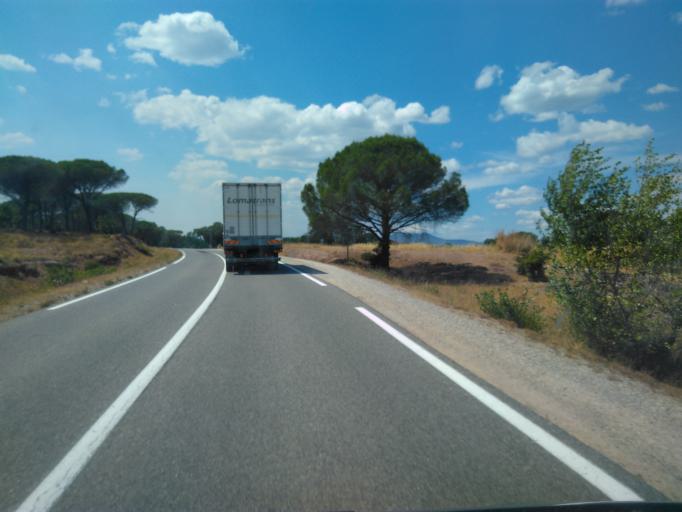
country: FR
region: Provence-Alpes-Cote d'Azur
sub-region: Departement du Var
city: La Garde-Freinet
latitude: 43.3507
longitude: 6.4251
